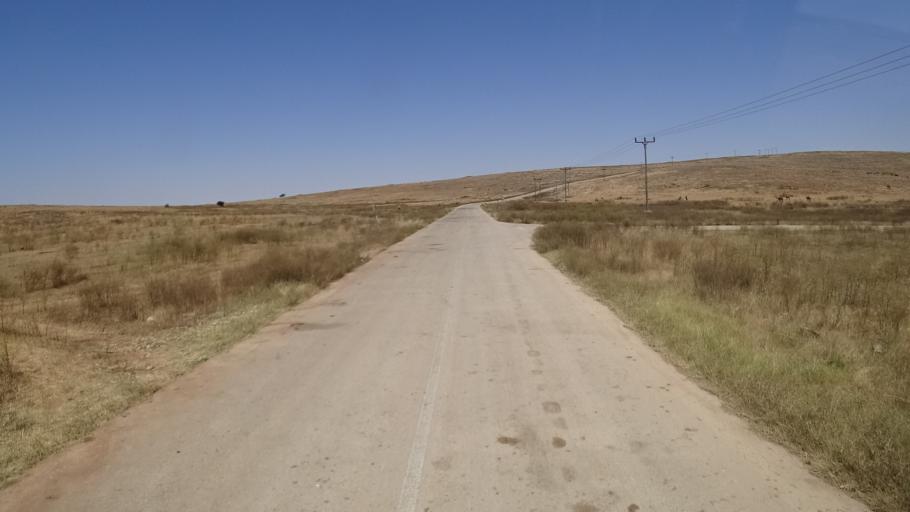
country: OM
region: Zufar
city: Salalah
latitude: 17.1546
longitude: 54.6181
